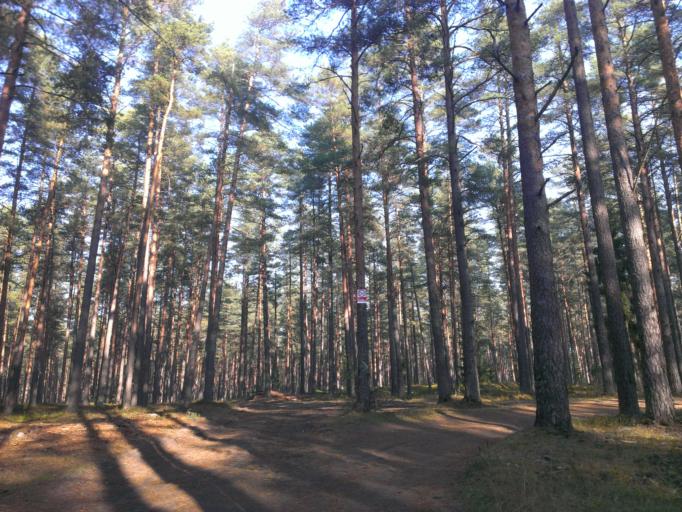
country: LV
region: Garkalne
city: Garkalne
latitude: 57.0167
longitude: 24.4660
